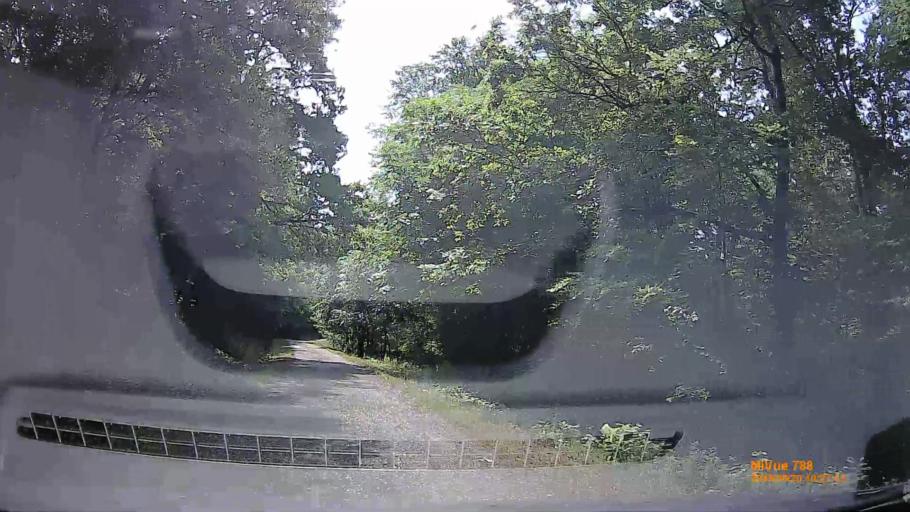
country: HU
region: Baranya
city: Mecseknadasd
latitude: 46.2071
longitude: 18.4896
